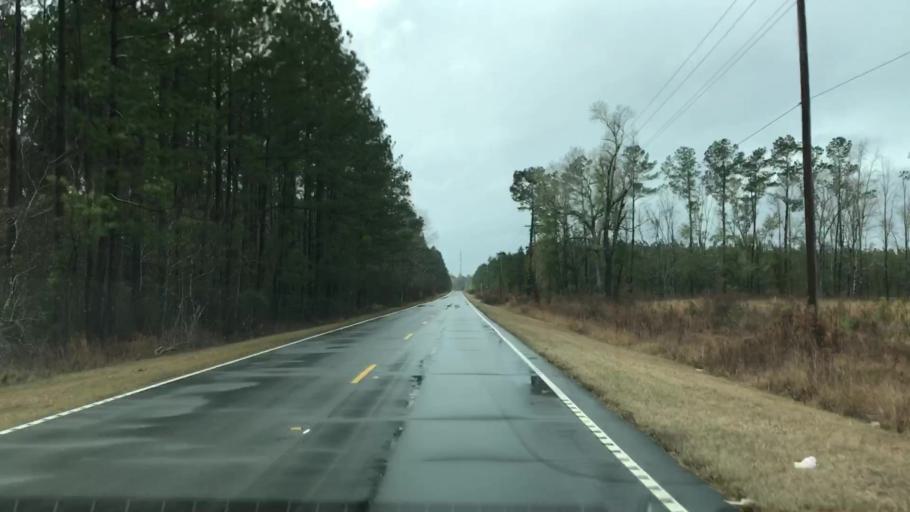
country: US
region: South Carolina
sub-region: Florence County
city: Johnsonville
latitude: 33.6760
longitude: -79.3384
